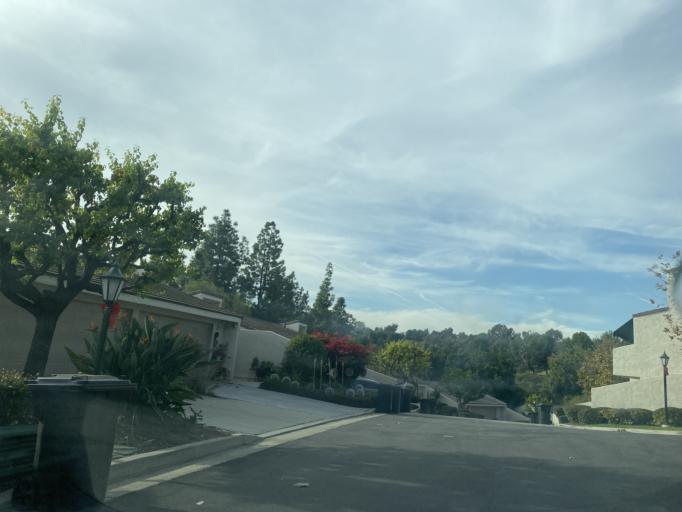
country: US
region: California
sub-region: Orange County
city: Brea
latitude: 33.8915
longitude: -117.8906
